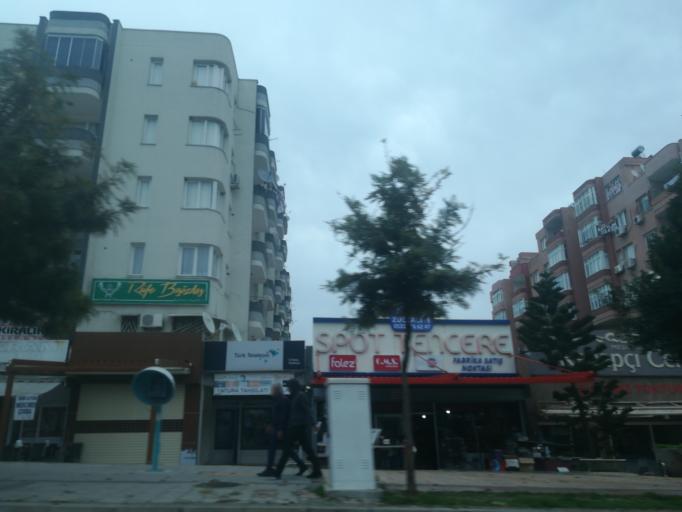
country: TR
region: Adana
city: Adana
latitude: 37.0343
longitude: 35.3081
